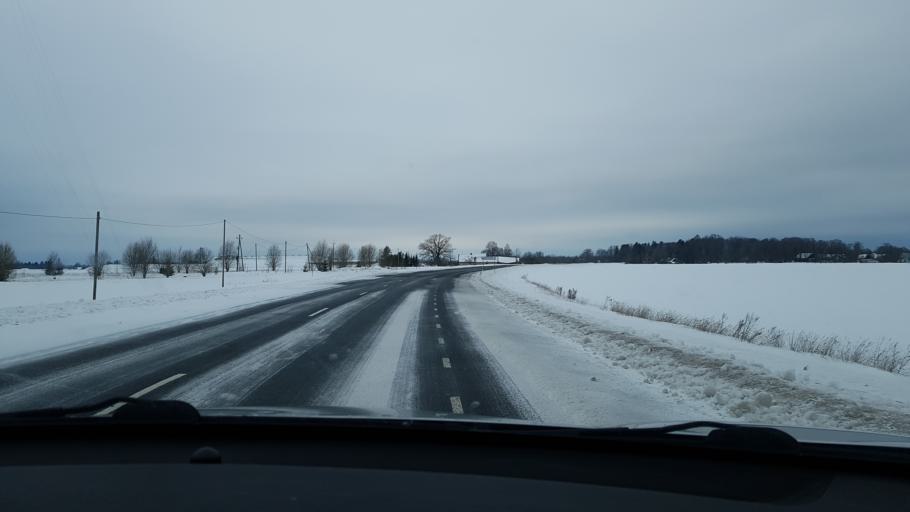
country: EE
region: Jaervamaa
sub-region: Jaerva-Jaani vald
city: Jarva-Jaani
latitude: 58.8960
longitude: 25.7596
